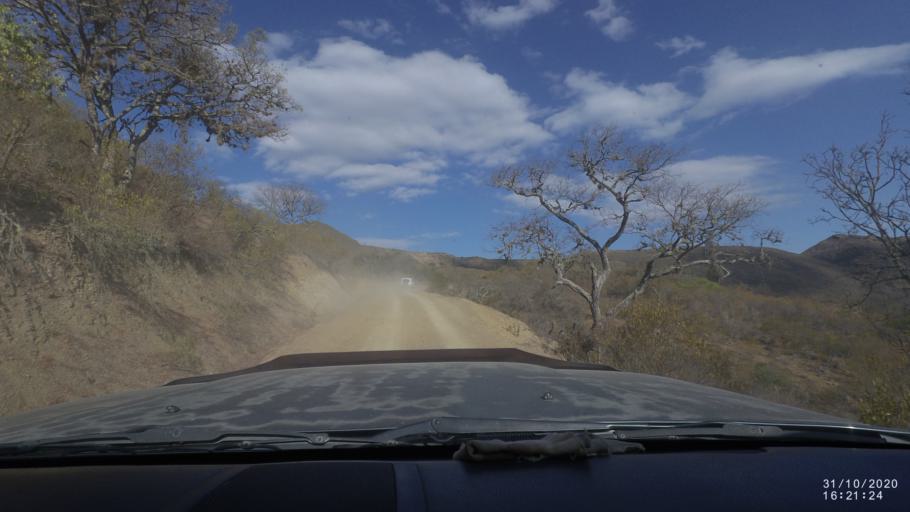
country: BO
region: Chuquisaca
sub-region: Provincia Zudanez
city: Mojocoya
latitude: -18.3987
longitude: -64.5980
